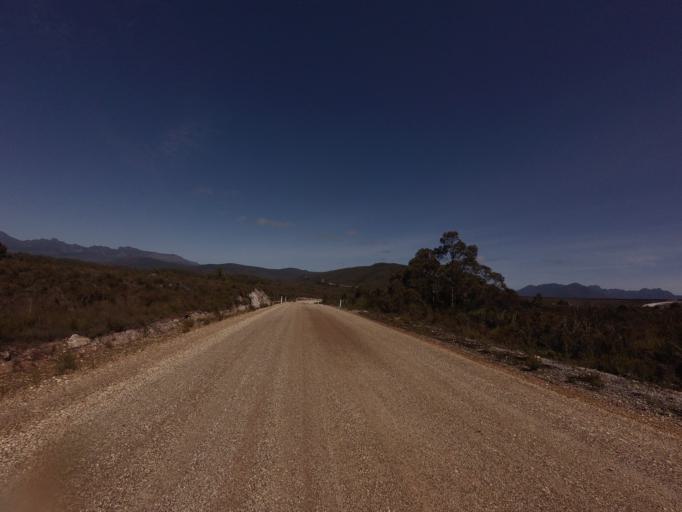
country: AU
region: Tasmania
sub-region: Huon Valley
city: Geeveston
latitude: -43.0318
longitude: 146.3039
